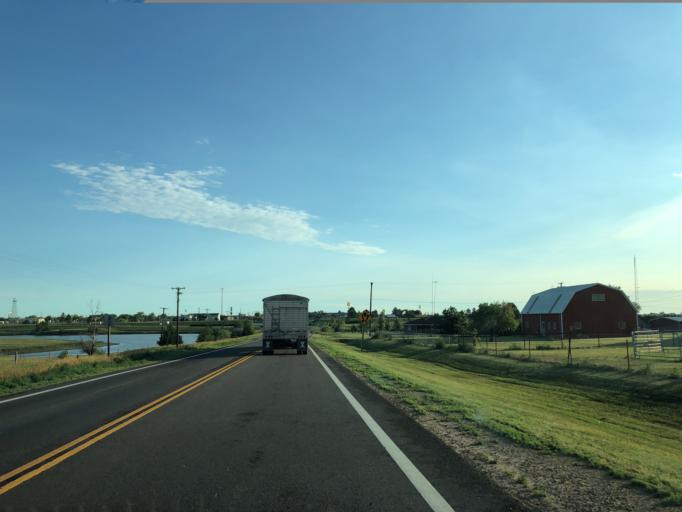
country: US
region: Kansas
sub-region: Russell County
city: Russell
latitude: 38.8588
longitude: -98.8545
